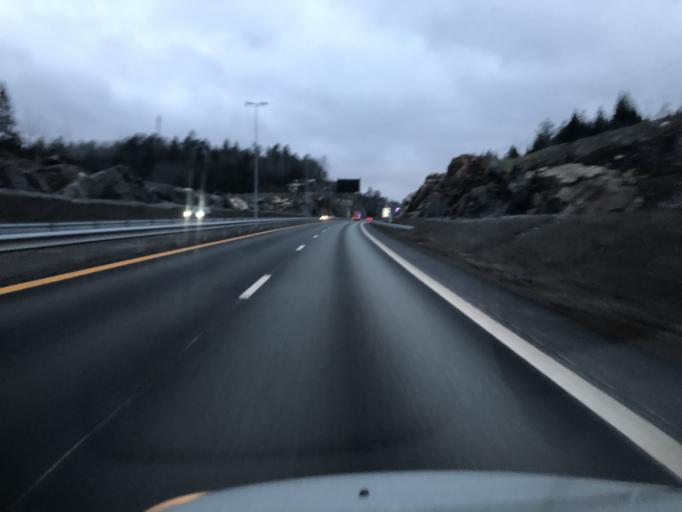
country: NO
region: Aust-Agder
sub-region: Arendal
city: Arendal
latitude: 58.5086
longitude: 8.8188
